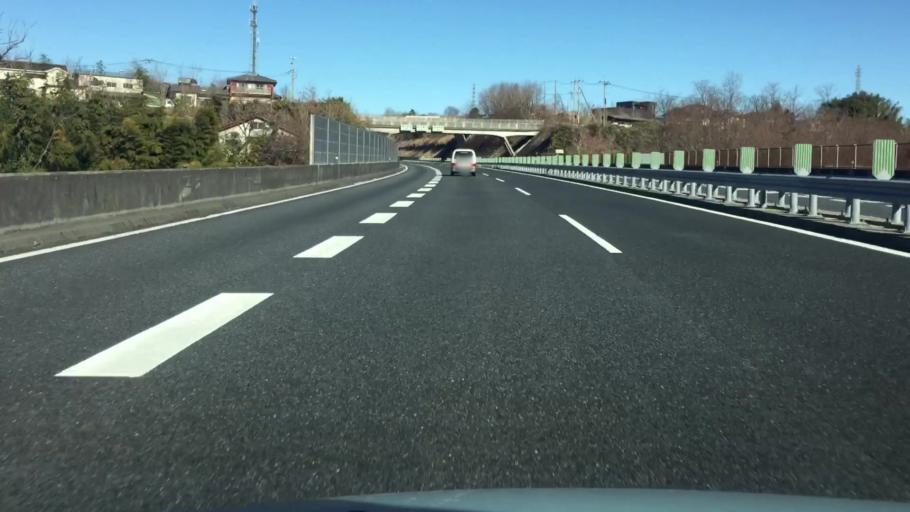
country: JP
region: Gunma
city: Shibukawa
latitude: 36.4909
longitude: 139.0309
